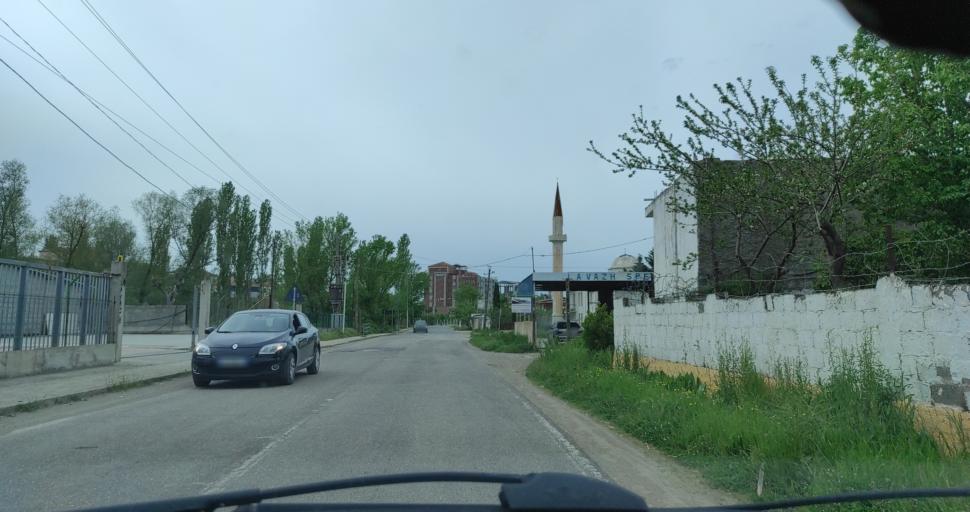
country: AL
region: Lezhe
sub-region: Rrethi i Kurbinit
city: Lac
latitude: 41.6187
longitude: 19.7113
